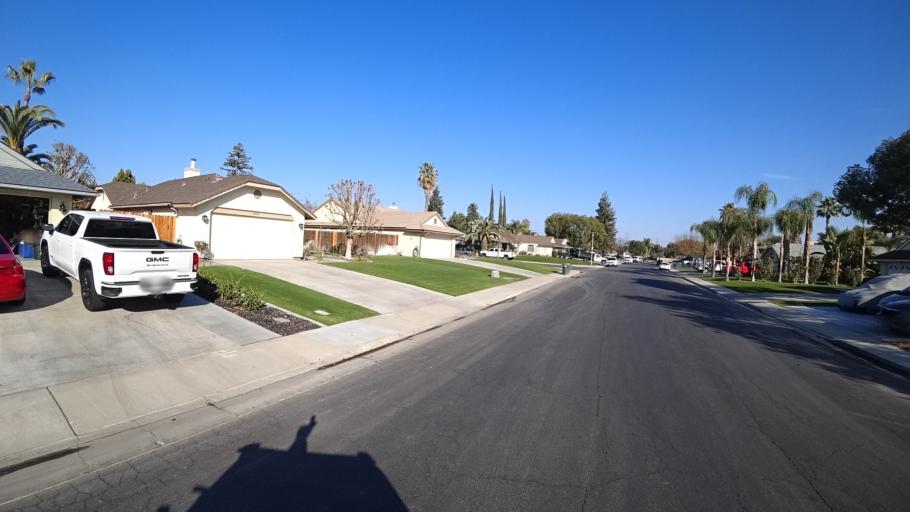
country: US
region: California
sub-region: Kern County
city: Greenacres
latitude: 35.3162
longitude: -119.1013
